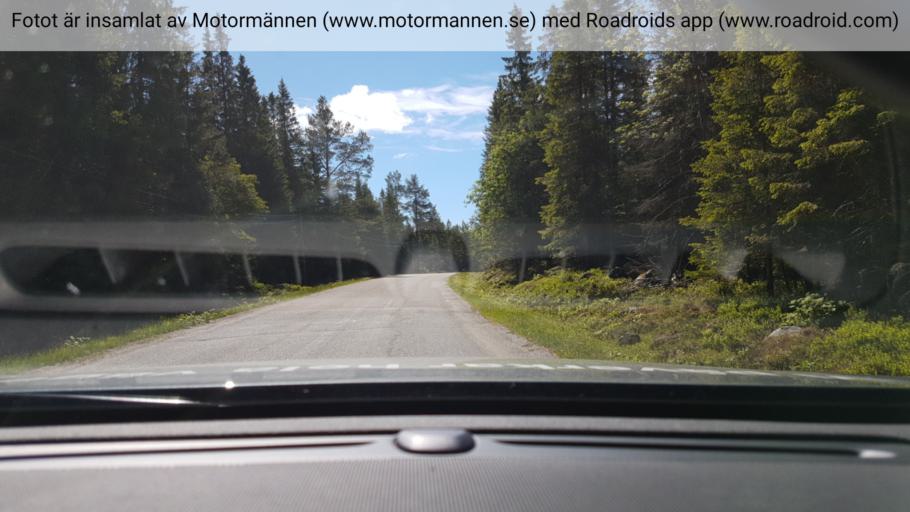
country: SE
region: Vaesterbotten
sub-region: Skelleftea Kommun
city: Burea
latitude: 64.4648
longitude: 21.5869
